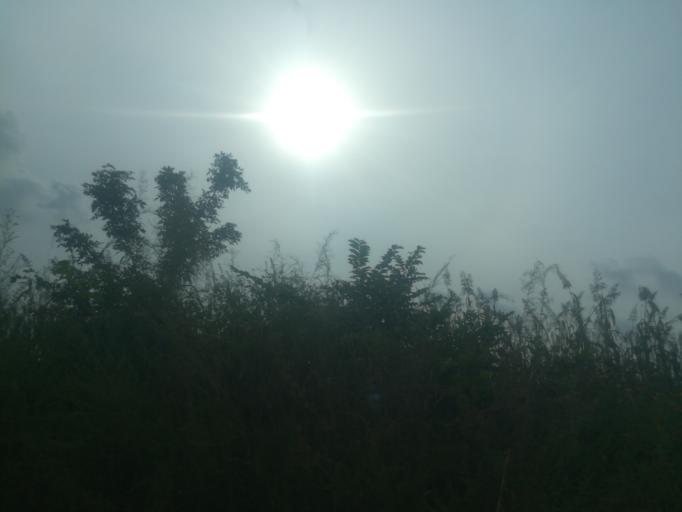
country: NG
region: Ogun
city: Ayetoro
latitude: 7.3162
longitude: 3.0700
